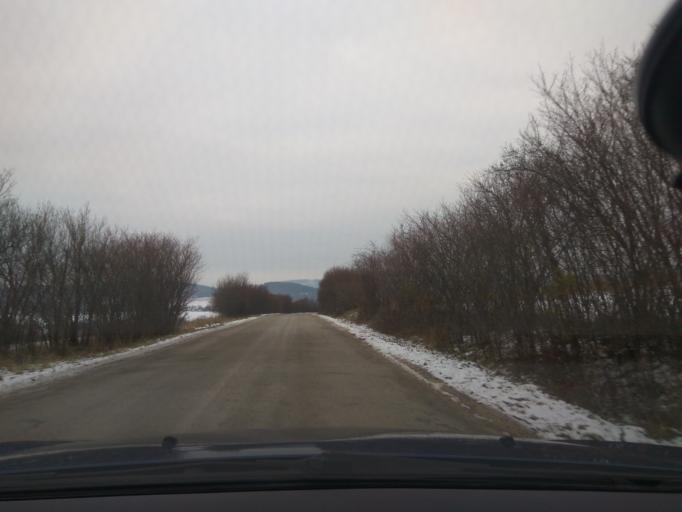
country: SK
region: Nitriansky
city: Stara Tura
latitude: 48.7975
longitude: 17.7183
